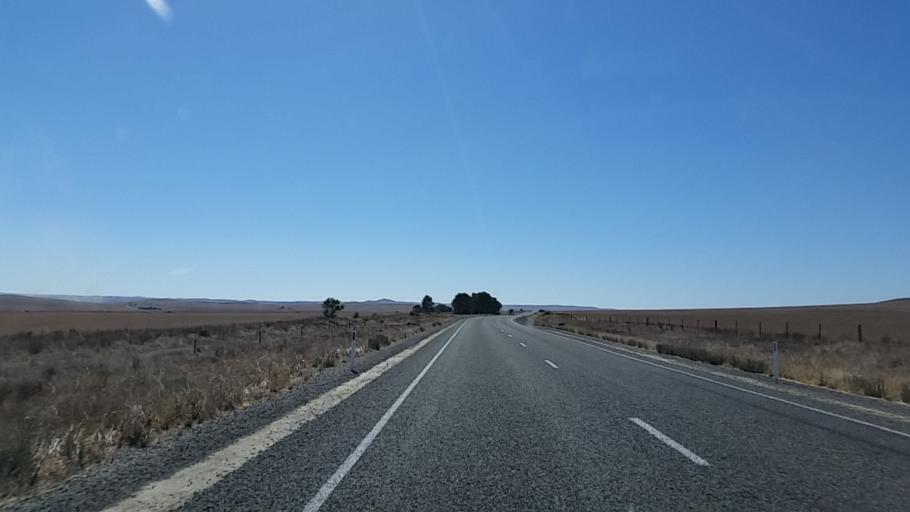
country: AU
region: South Australia
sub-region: Northern Areas
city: Jamestown
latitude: -33.3010
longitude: 138.8751
